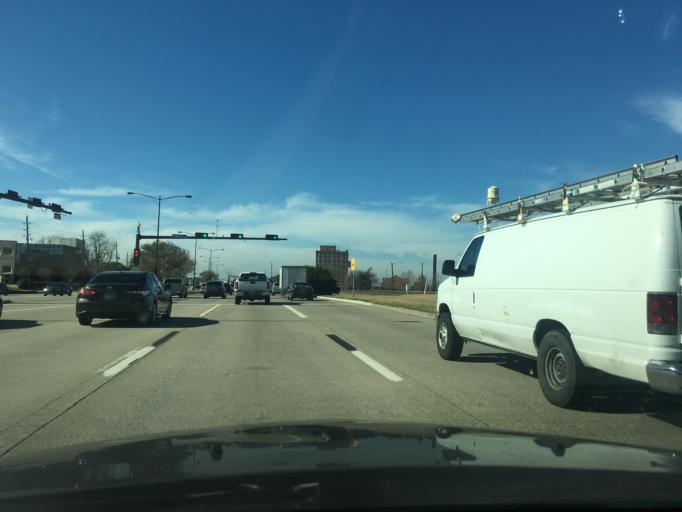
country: US
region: Texas
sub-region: Fort Bend County
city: Sugar Land
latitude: 29.6213
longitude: -95.6291
